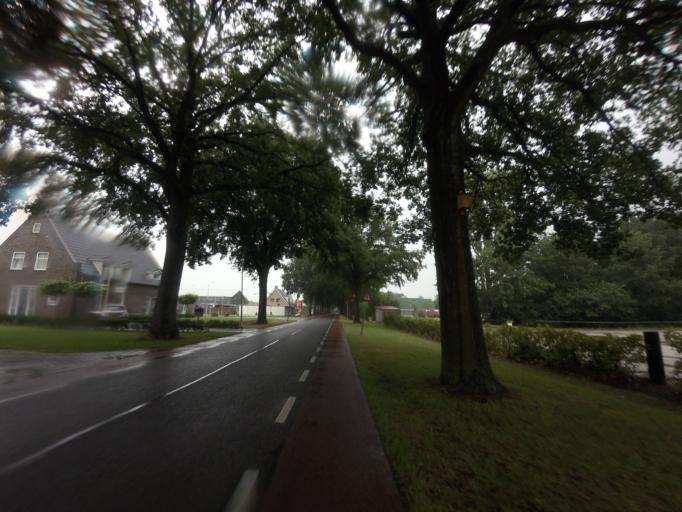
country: NL
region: Drenthe
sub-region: Gemeente Hoogeveen
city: Hoogeveen
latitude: 52.6066
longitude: 6.3944
